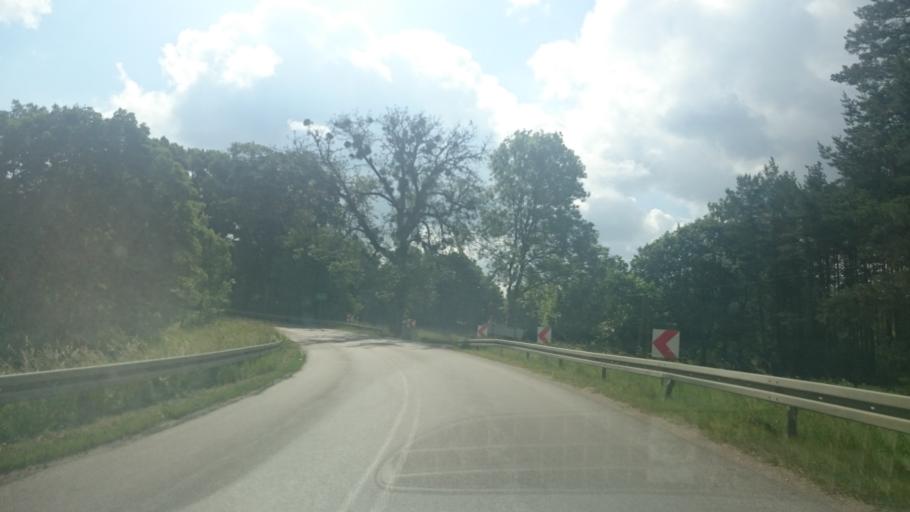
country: PL
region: Pomeranian Voivodeship
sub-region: Powiat starogardzki
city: Kaliska
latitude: 53.9691
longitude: 18.2451
